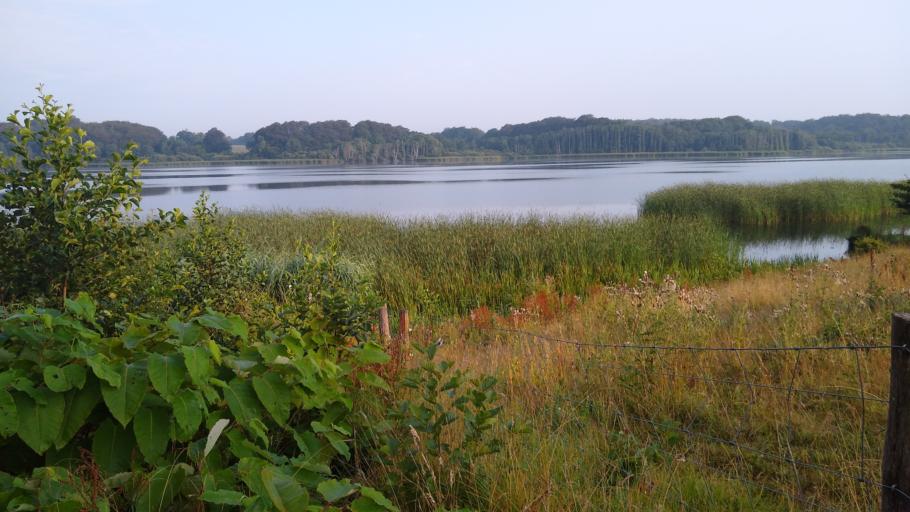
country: DK
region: South Denmark
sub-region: Fredericia Kommune
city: Fredericia
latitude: 55.6084
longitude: 9.7108
